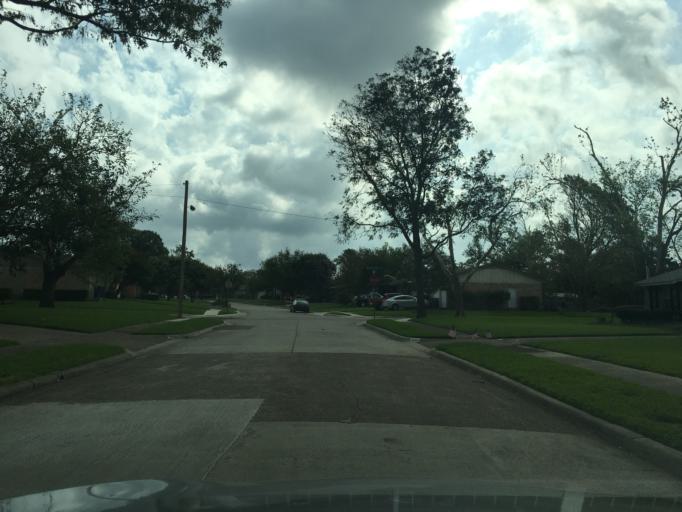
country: US
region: Texas
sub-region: Dallas County
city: Richardson
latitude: 32.8993
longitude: -96.7547
